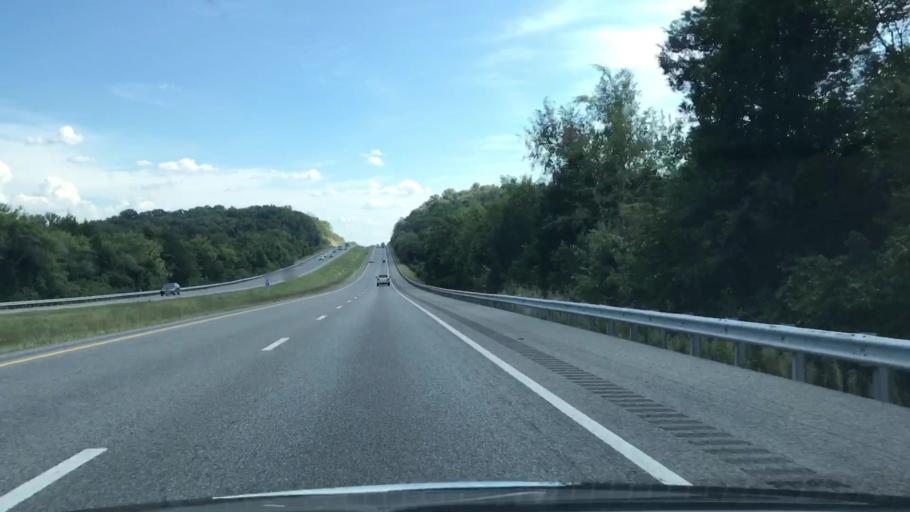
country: US
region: Alabama
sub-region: Limestone County
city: Ardmore
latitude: 35.0976
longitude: -86.8853
